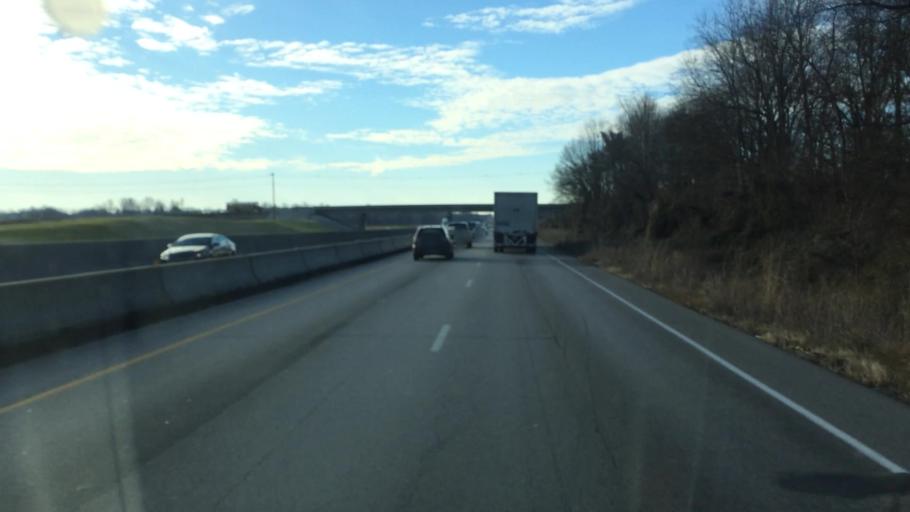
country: US
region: Kentucky
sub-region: Hardin County
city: Elizabethtown
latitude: 37.5759
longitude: -85.8733
